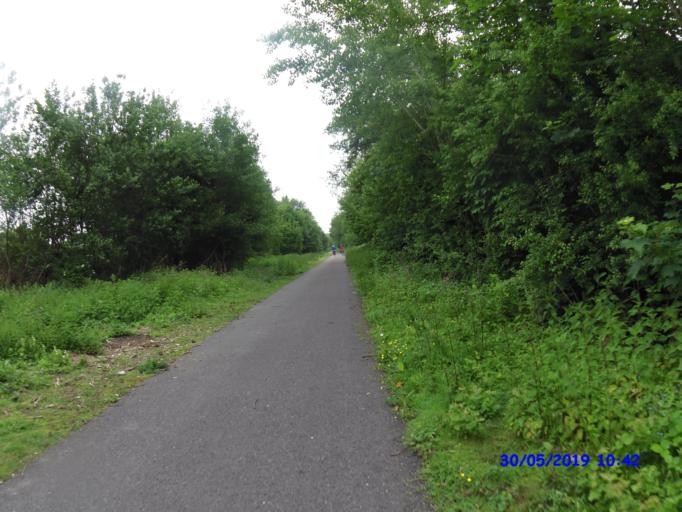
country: BE
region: Wallonia
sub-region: Province du Hainaut
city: Beaumont
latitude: 50.2427
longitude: 4.2500
